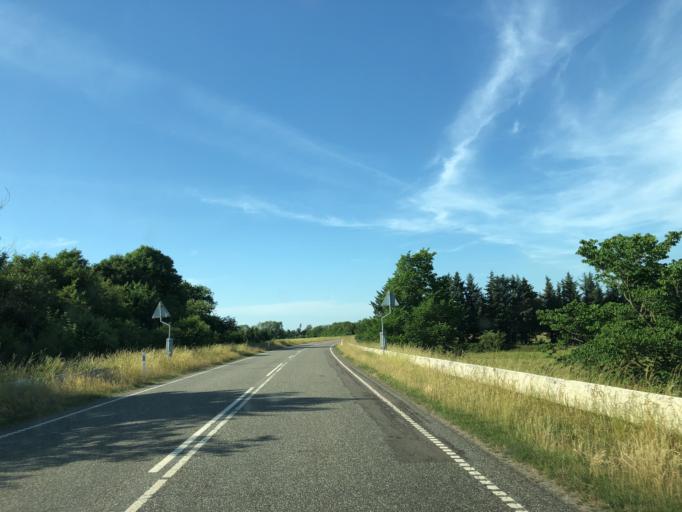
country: DK
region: Central Jutland
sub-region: Holstebro Kommune
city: Ulfborg
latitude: 56.3697
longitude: 8.4404
